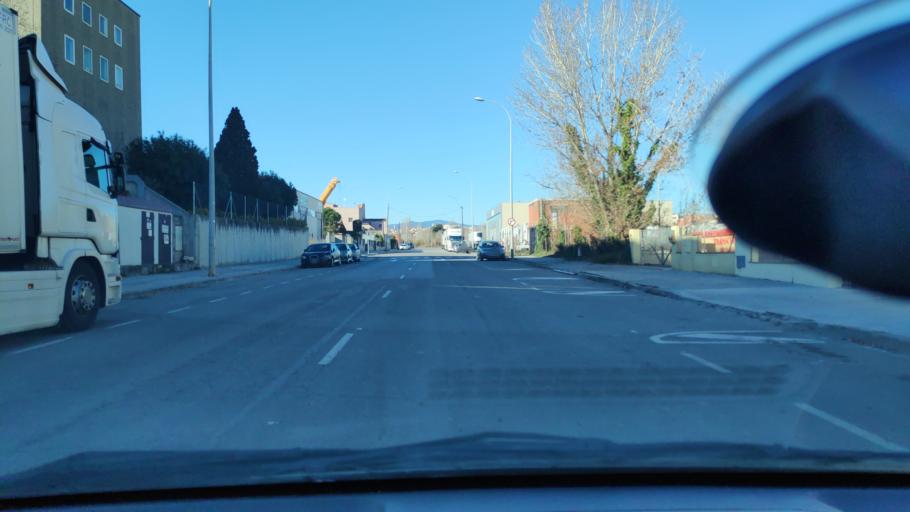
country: ES
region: Catalonia
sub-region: Provincia de Barcelona
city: Sant Quirze del Valles
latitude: 41.5229
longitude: 2.0916
